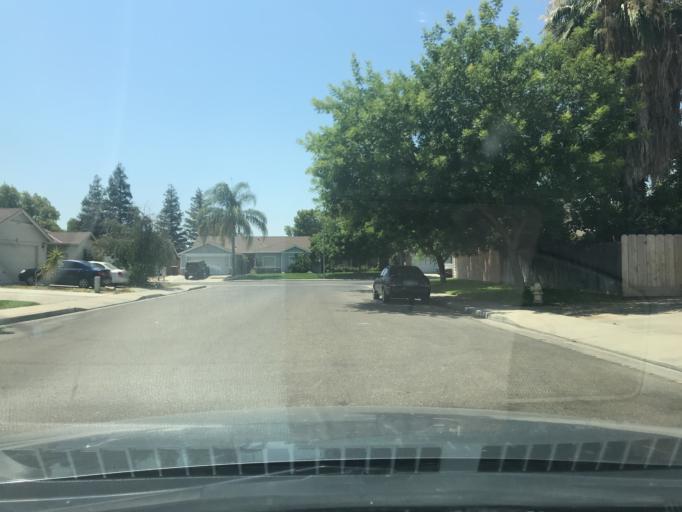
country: US
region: California
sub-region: Merced County
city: Atwater
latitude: 37.3509
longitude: -120.5838
